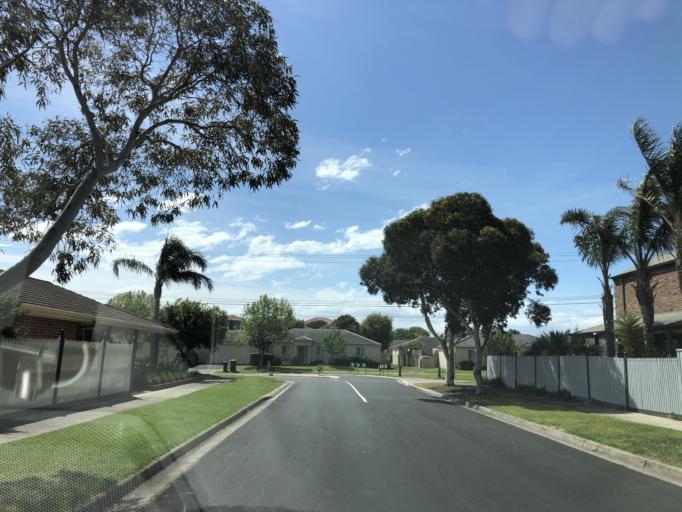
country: AU
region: Victoria
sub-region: Kingston
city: Patterson Lakes
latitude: -38.0708
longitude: 145.1418
